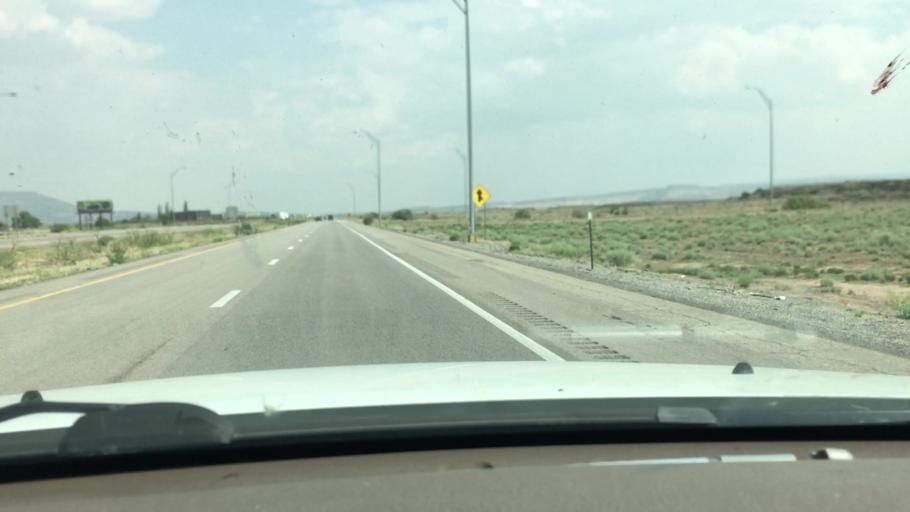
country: US
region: New Mexico
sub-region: Cibola County
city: Grants
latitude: 35.1225
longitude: -107.8275
